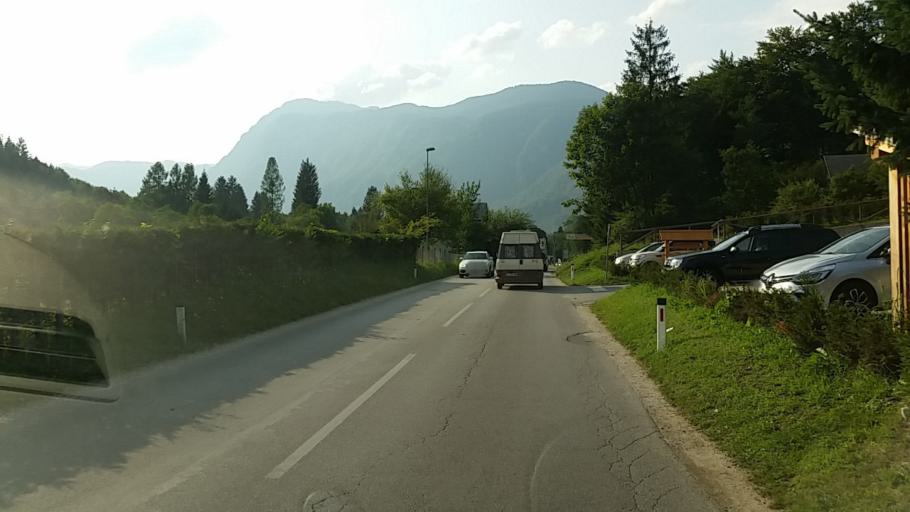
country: SI
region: Bohinj
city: Bohinjska Bistrica
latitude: 46.2749
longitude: 13.8911
